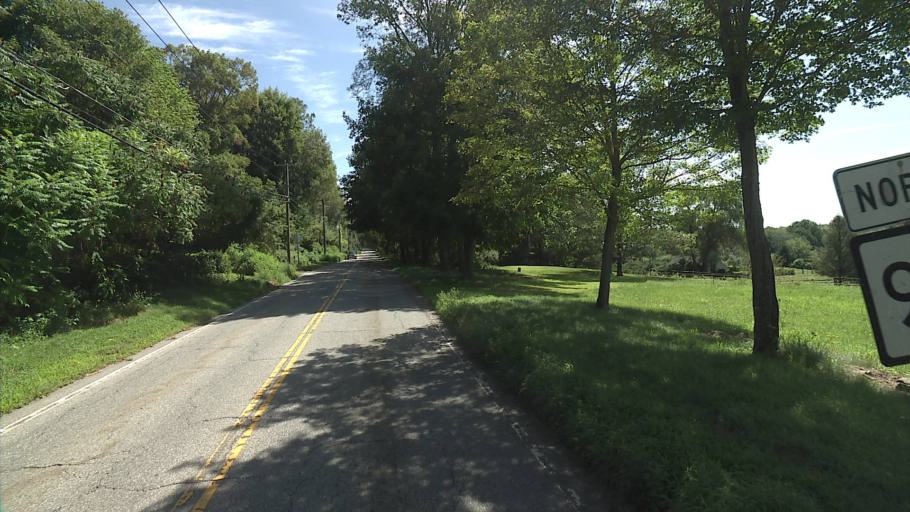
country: US
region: Connecticut
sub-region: Windham County
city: South Woodstock
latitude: 41.8953
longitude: -71.9748
